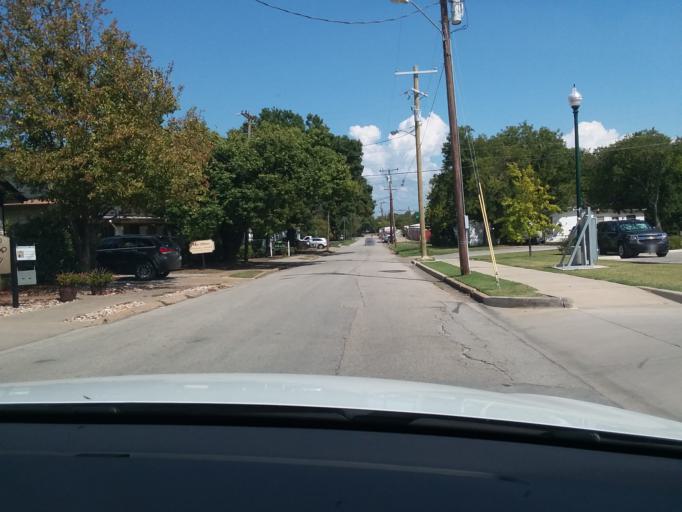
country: US
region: Texas
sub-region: Collin County
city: McKinney
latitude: 33.2006
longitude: -96.6147
